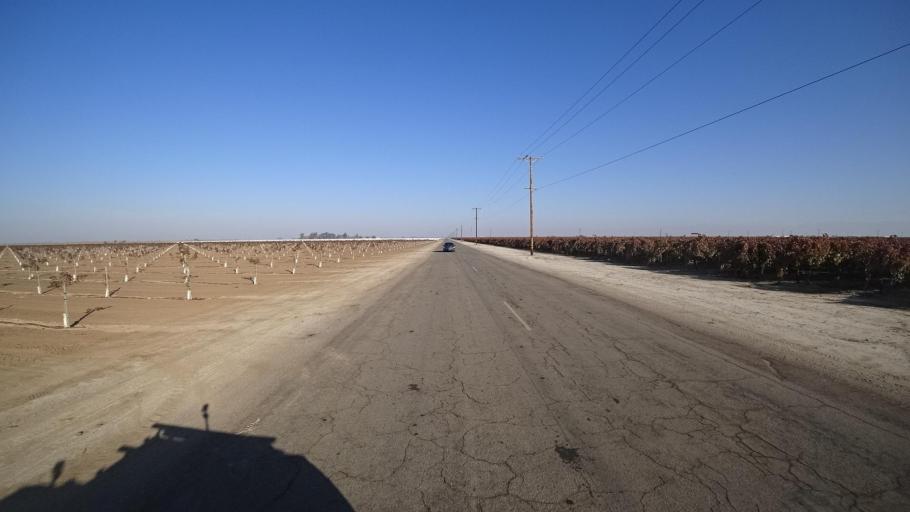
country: US
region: California
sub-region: Kern County
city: McFarland
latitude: 35.7293
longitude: -119.1695
